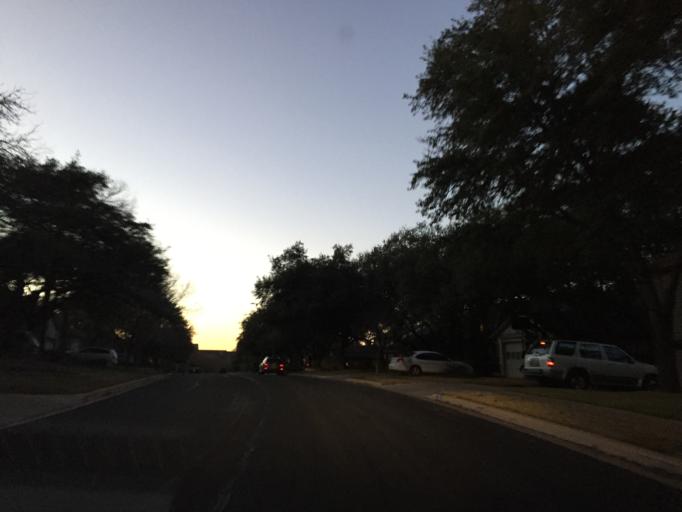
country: US
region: Texas
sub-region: Travis County
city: Wells Branch
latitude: 30.4003
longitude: -97.6936
